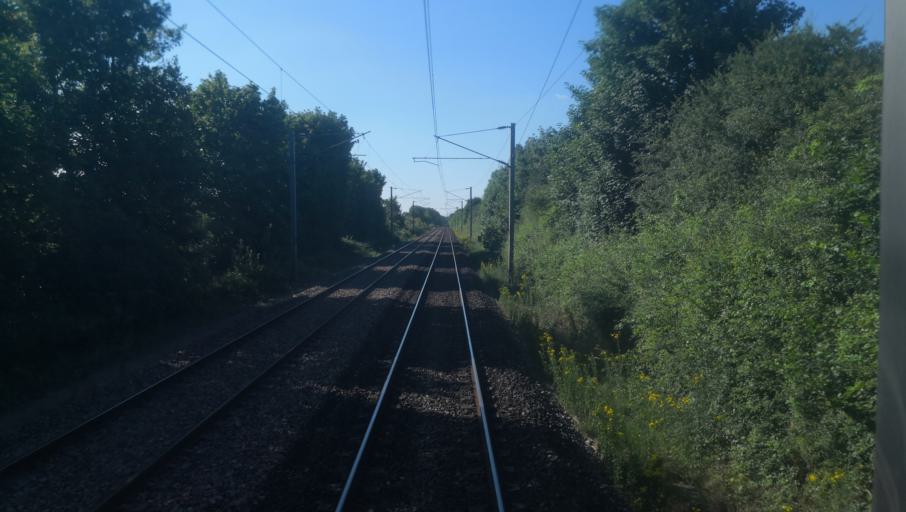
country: FR
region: Bourgogne
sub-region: Departement de la Nievre
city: Neuvy-sur-Loire
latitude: 47.5373
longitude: 2.8619
